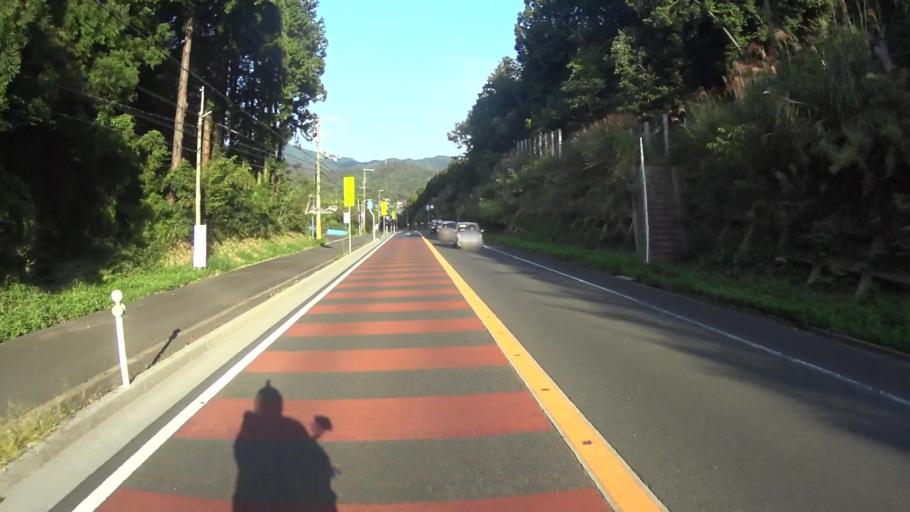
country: JP
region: Hyogo
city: Toyooka
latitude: 35.5837
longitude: 134.9565
